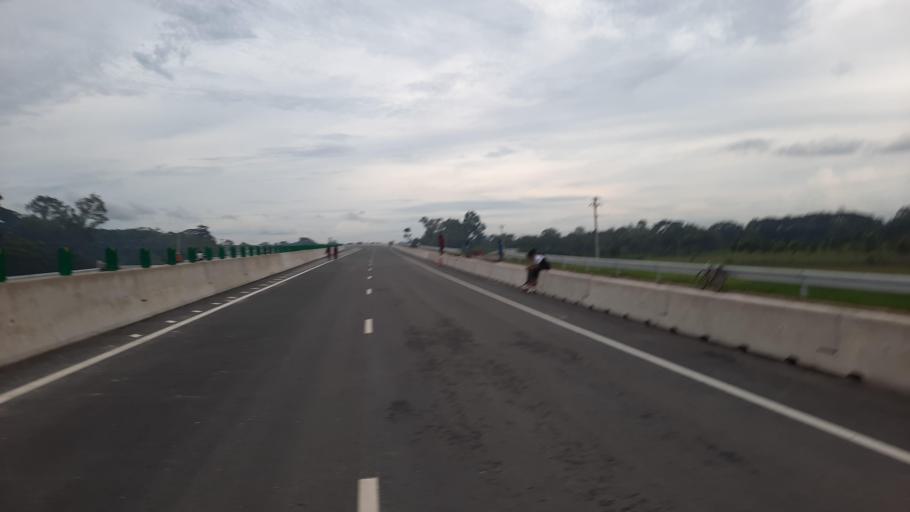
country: BD
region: Khulna
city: Kalia
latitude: 23.1901
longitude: 89.6943
